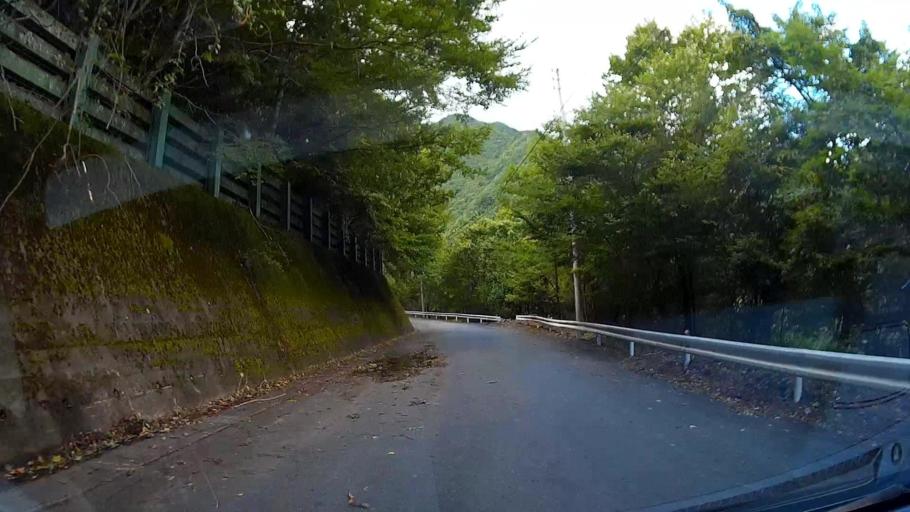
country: JP
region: Shizuoka
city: Shizuoka-shi
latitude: 35.3022
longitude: 138.2163
